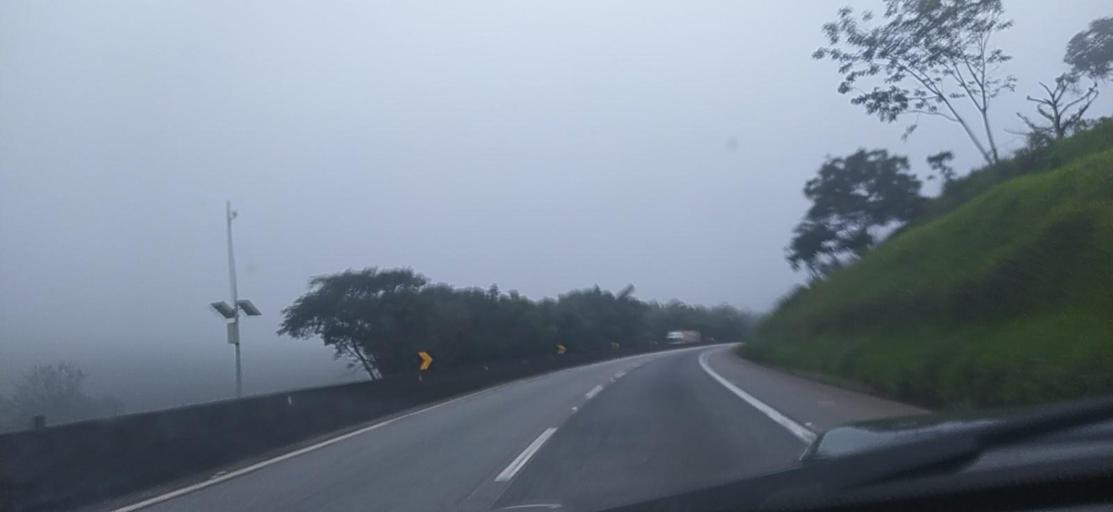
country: BR
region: Minas Gerais
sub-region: Tres Coracoes
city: Tres Coracoes
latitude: -21.5740
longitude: -45.2424
